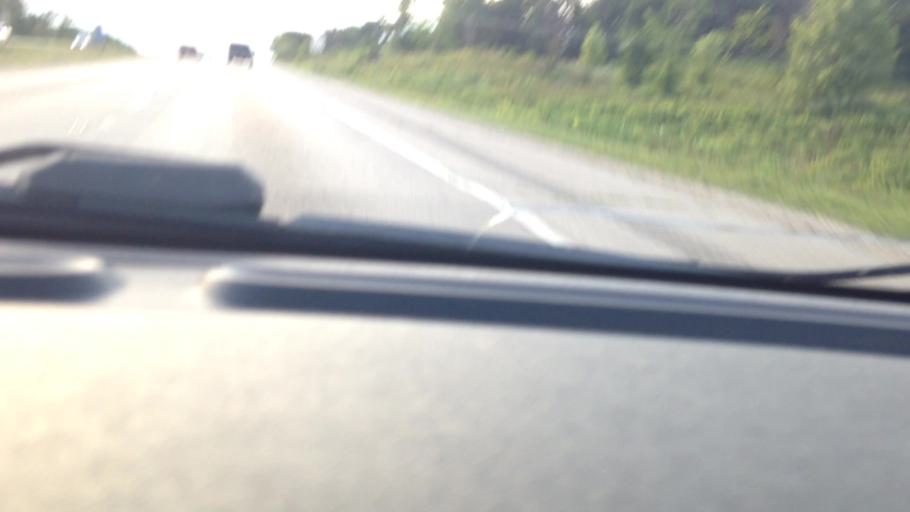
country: US
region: Wisconsin
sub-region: Washington County
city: Slinger
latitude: 43.3306
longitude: -88.2586
